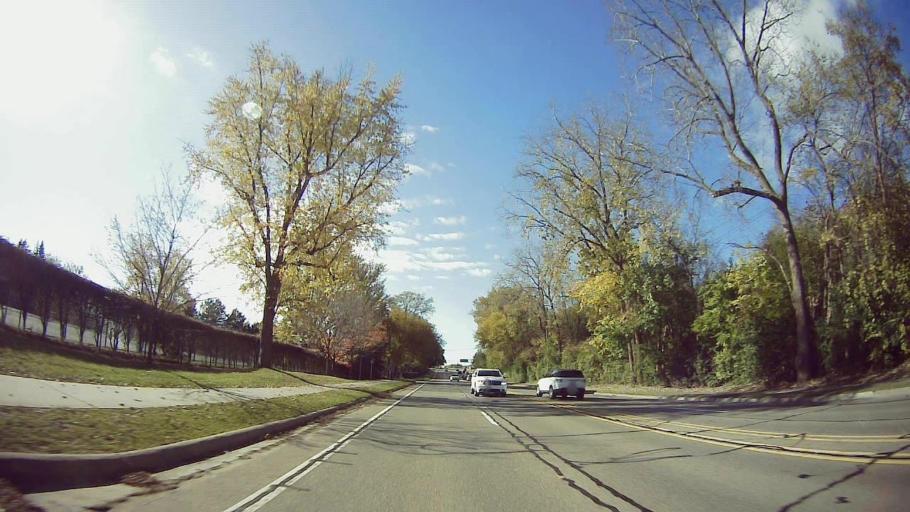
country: US
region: Michigan
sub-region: Oakland County
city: Bingham Farms
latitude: 42.5449
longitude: -83.2785
